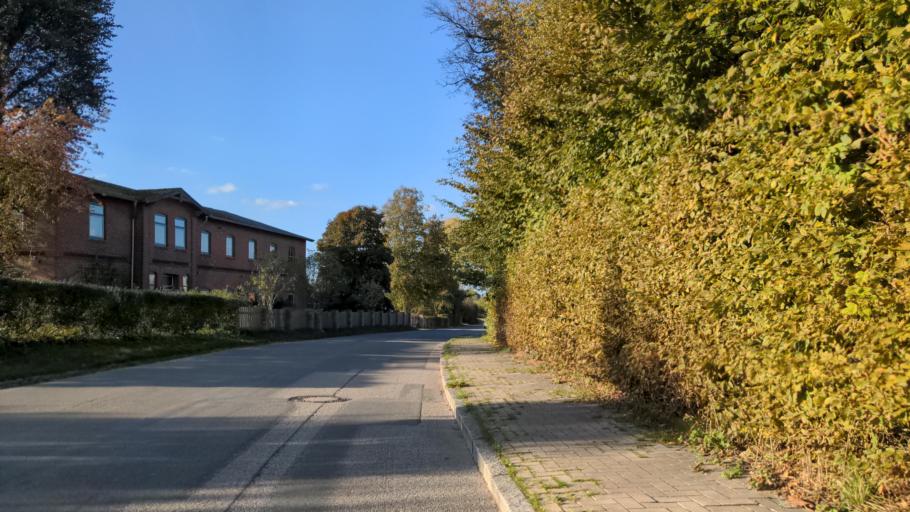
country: DE
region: Schleswig-Holstein
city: Strukdorf
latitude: 53.9498
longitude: 10.5265
